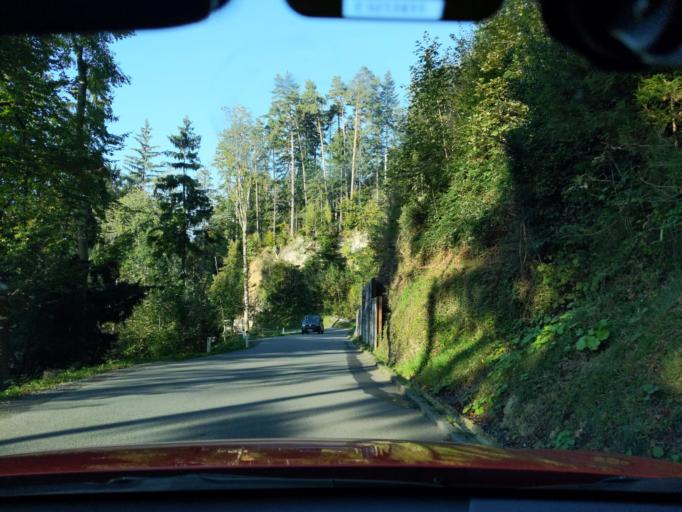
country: AT
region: Vorarlberg
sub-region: Politischer Bezirk Bregenz
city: Lochau
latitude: 47.5218
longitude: 9.7598
